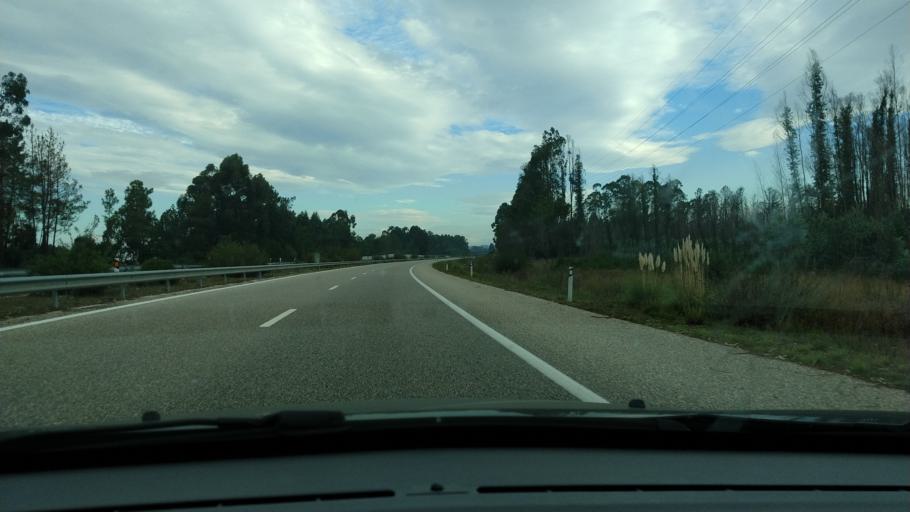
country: PT
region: Coimbra
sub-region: Mira
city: Mira
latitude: 40.4773
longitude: -8.6885
